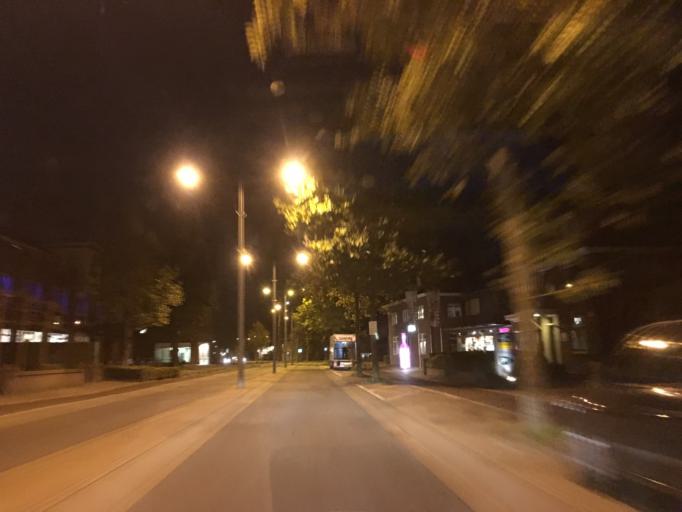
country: NL
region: North Brabant
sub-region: Gemeente Cuijk
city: Cuijk
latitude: 51.7831
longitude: 5.8517
